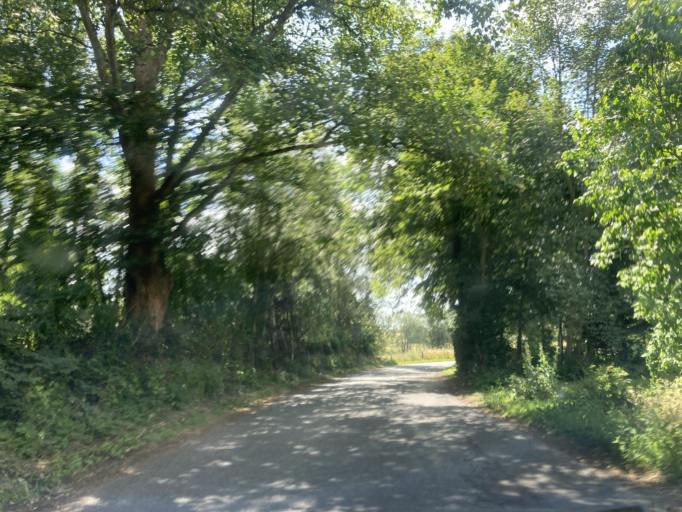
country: DK
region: Zealand
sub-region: Faxe Kommune
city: Haslev
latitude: 55.3572
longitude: 11.9523
